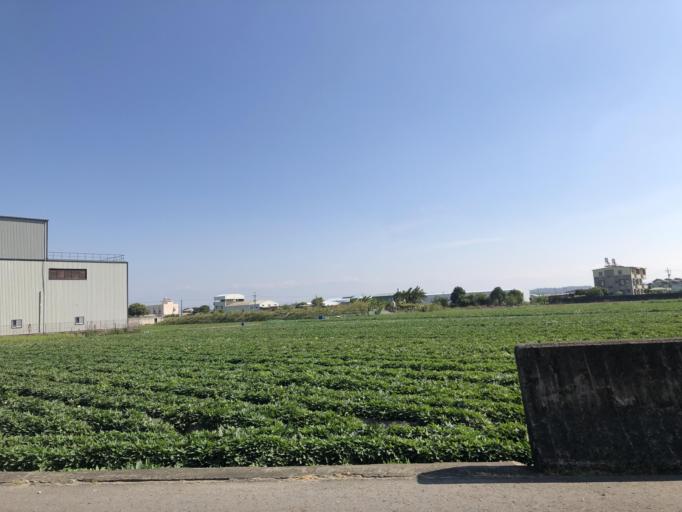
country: TW
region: Taiwan
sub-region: Tainan
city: Tainan
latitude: 23.0205
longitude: 120.2893
